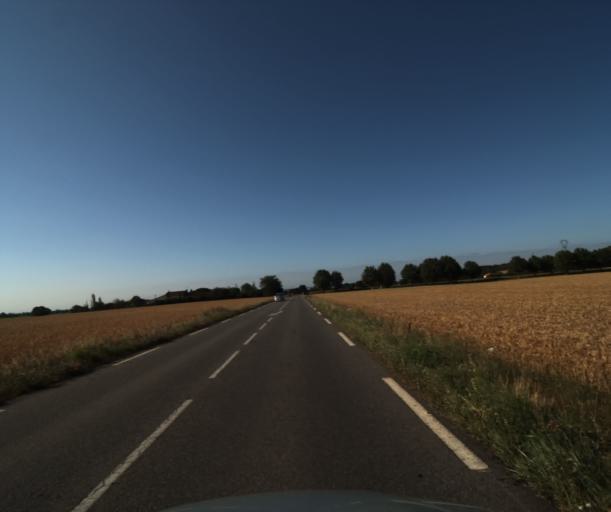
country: FR
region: Midi-Pyrenees
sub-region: Departement de la Haute-Garonne
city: Lagardelle-sur-Leze
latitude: 43.4355
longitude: 1.3786
